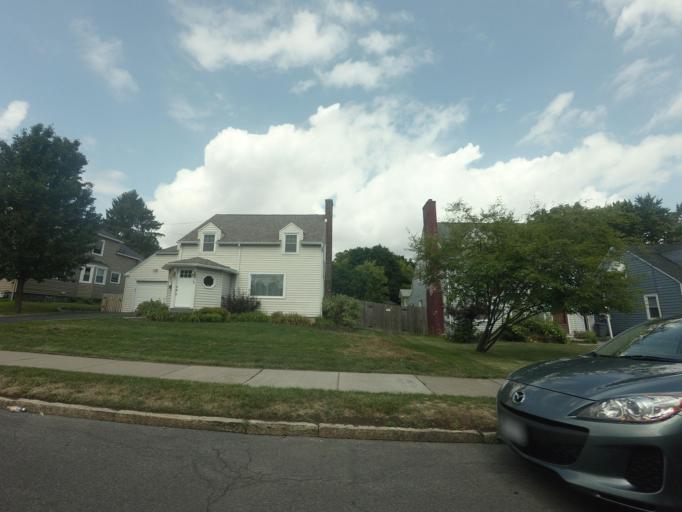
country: US
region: New York
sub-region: Onondaga County
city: Syracuse
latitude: 43.0305
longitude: -76.1179
